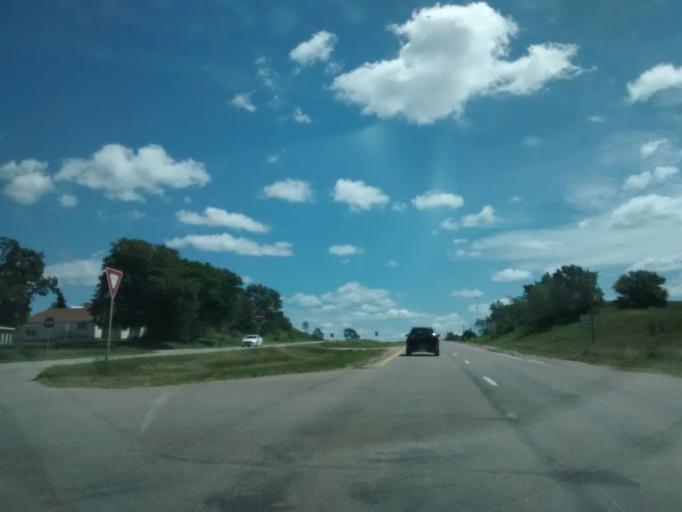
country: US
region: Iowa
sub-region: Woodbury County
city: Moville
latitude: 42.4751
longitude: -96.1747
